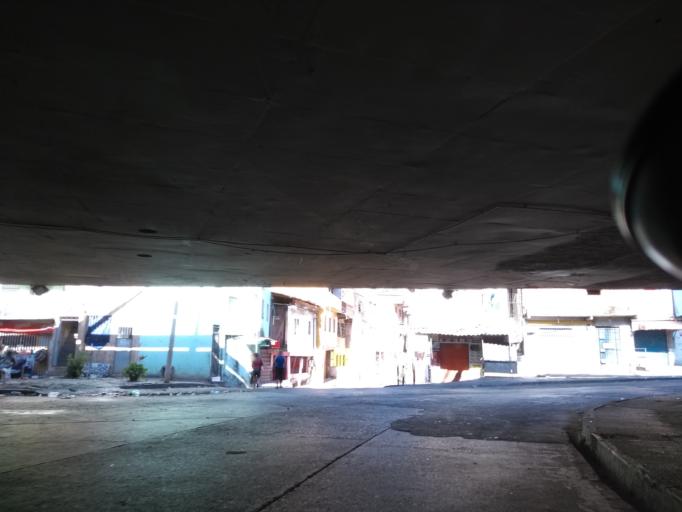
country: BR
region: Bahia
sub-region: Salvador
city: Salvador
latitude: -12.9833
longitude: -38.5109
